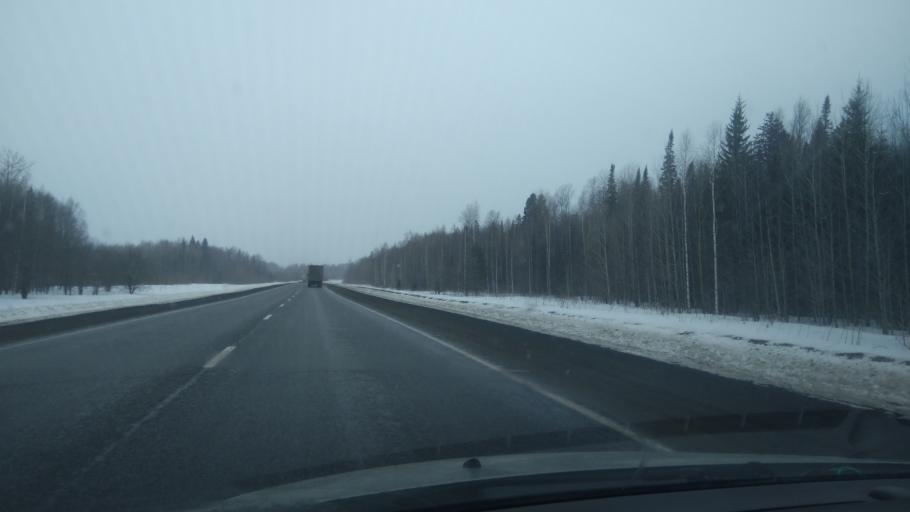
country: RU
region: Perm
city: Suksun
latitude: 57.1599
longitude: 57.1797
